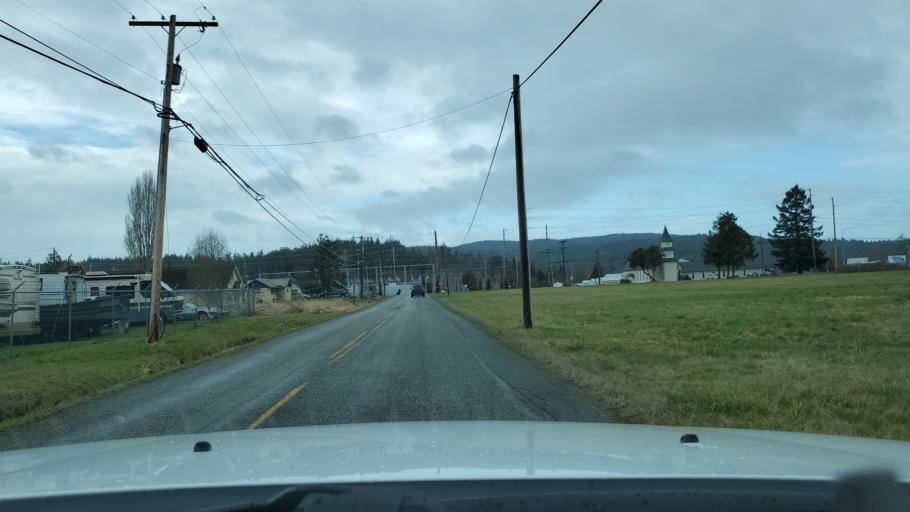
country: US
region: Washington
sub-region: Skagit County
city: Anacortes
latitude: 48.4585
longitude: -122.5578
